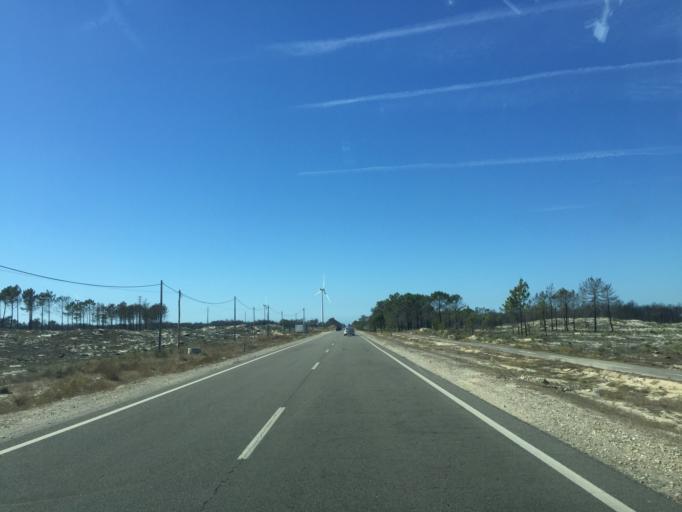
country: PT
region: Coimbra
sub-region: Mira
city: Mira
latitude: 40.3230
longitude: -8.7927
